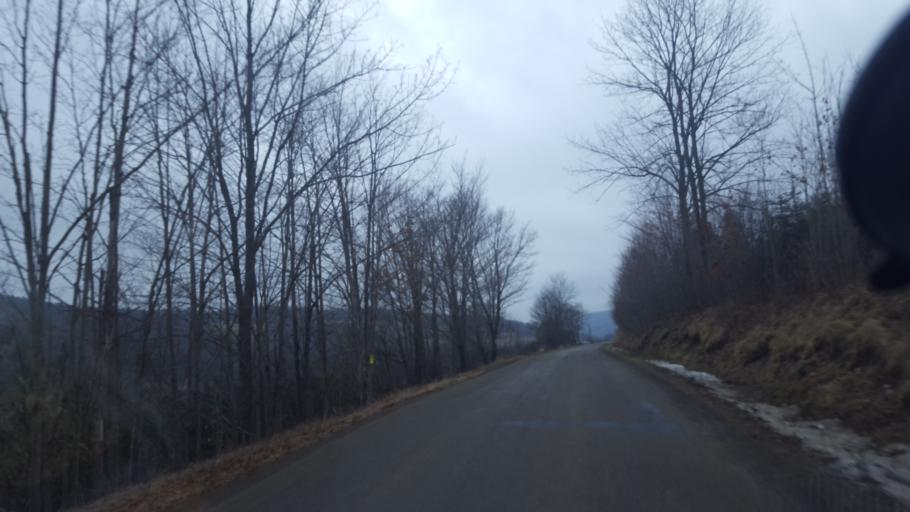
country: US
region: Pennsylvania
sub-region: Tioga County
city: Westfield
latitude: 41.9551
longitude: -77.6968
